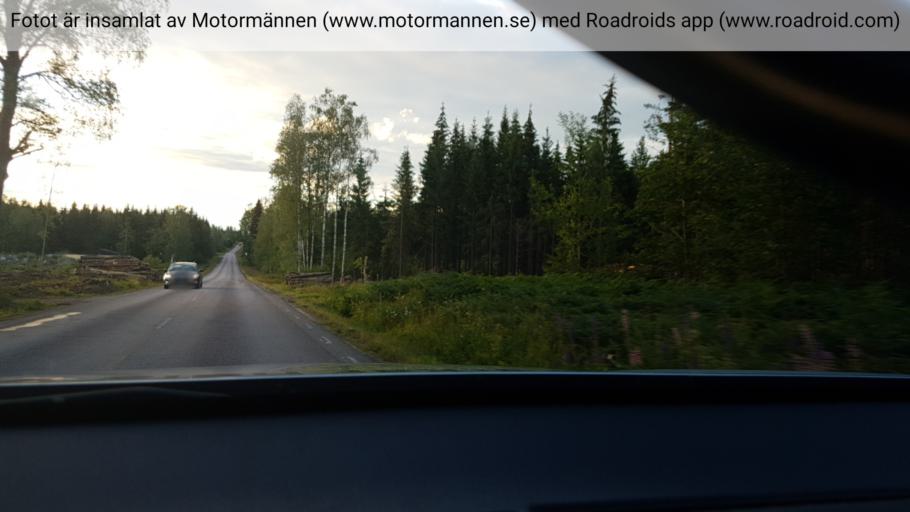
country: SE
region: Vaermland
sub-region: Torsby Kommun
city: Torsby
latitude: 60.1090
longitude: 13.0672
